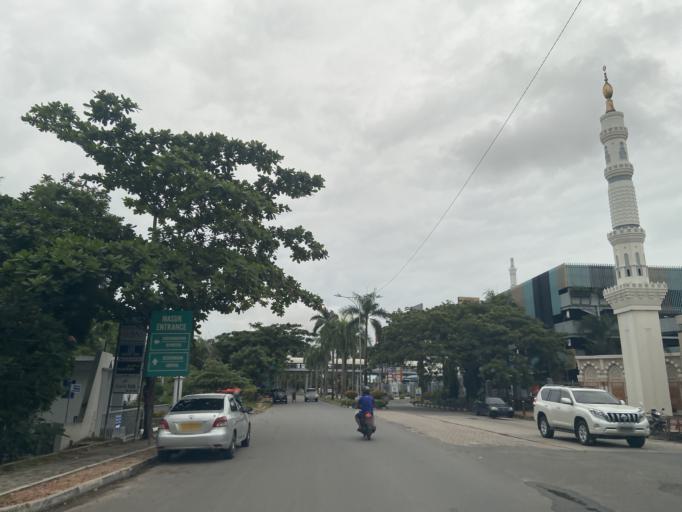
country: SG
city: Singapore
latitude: 1.1300
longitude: 104.0543
